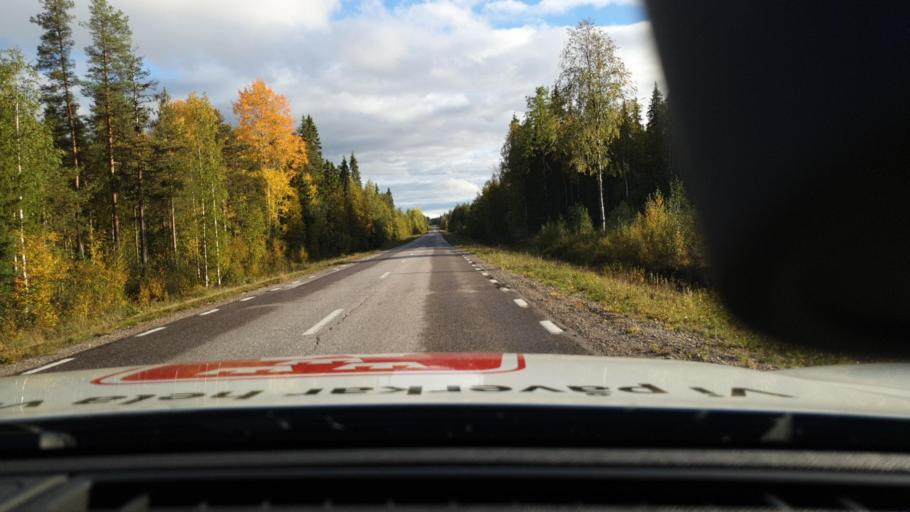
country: SE
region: Norrbotten
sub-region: Overkalix Kommun
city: OEverkalix
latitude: 66.6975
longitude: 22.6680
